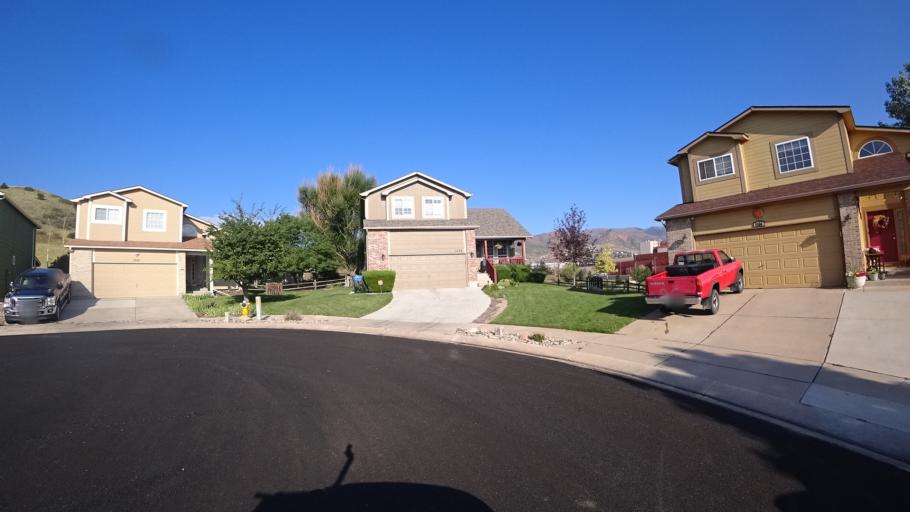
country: US
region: Colorado
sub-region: El Paso County
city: Manitou Springs
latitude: 38.8922
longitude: -104.8579
